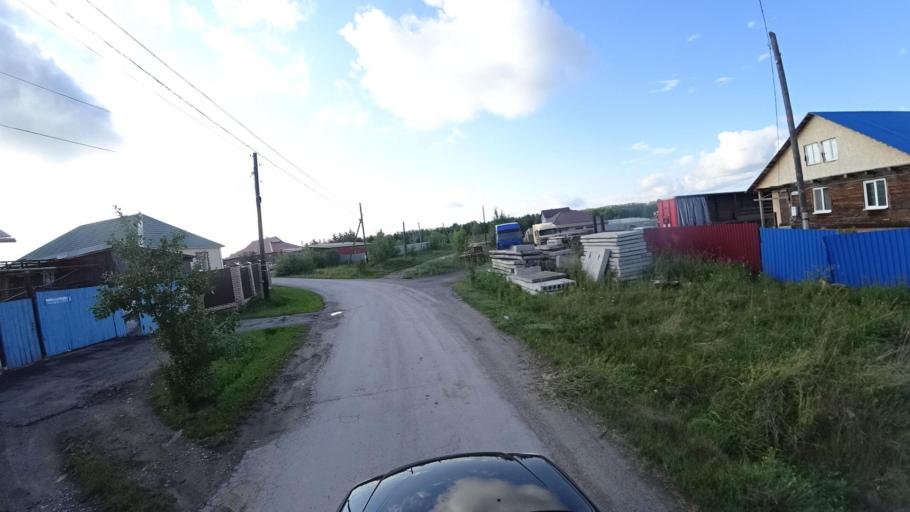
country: RU
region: Sverdlovsk
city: Obukhovskoye
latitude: 56.8506
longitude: 62.6524
